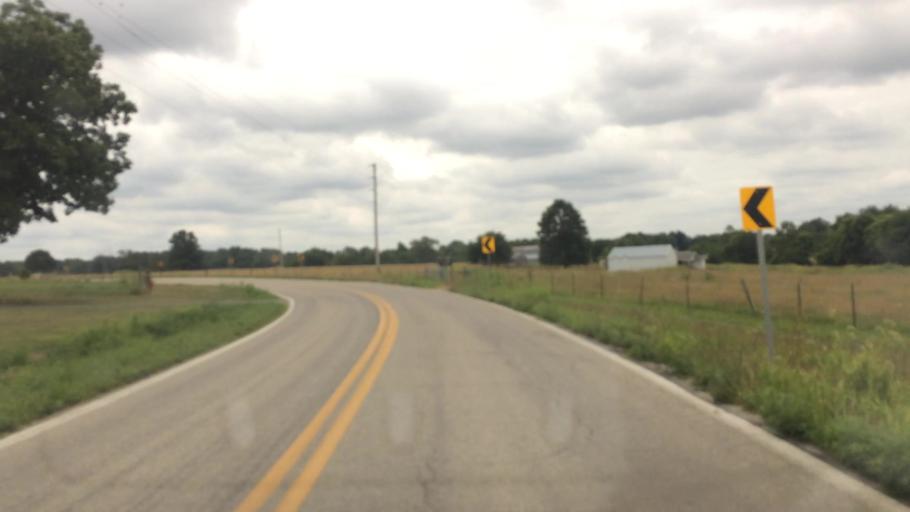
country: US
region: Missouri
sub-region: Greene County
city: Strafford
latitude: 37.2968
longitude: -93.1202
